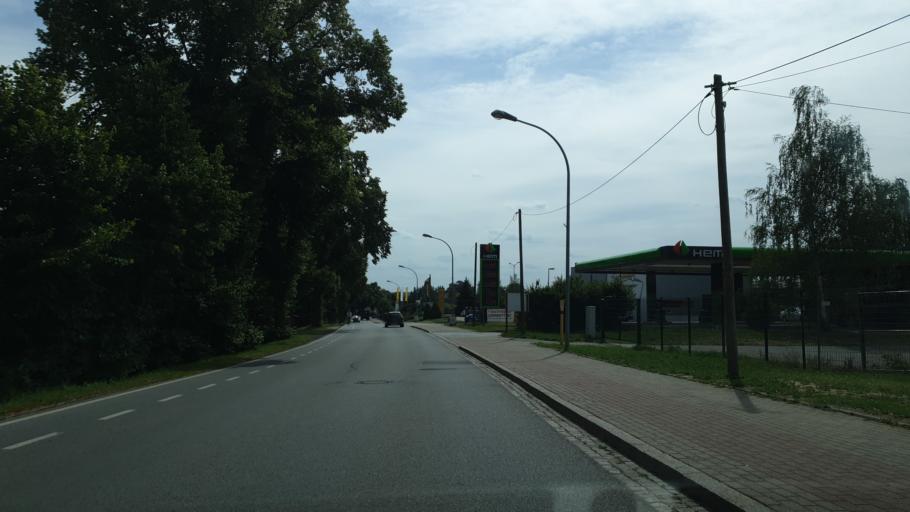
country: DE
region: Saxony
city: Oberlungwitz
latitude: 50.7914
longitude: 12.6978
